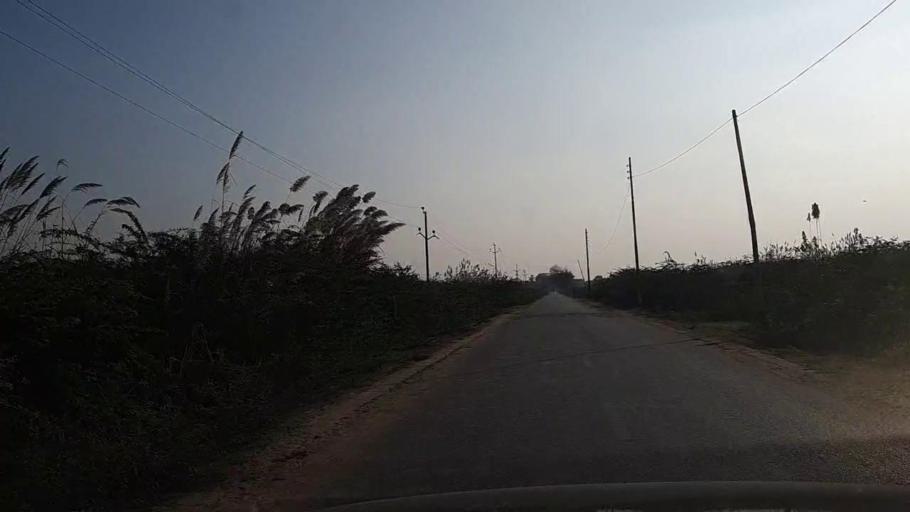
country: PK
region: Sindh
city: Gharo
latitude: 24.7829
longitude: 67.5122
